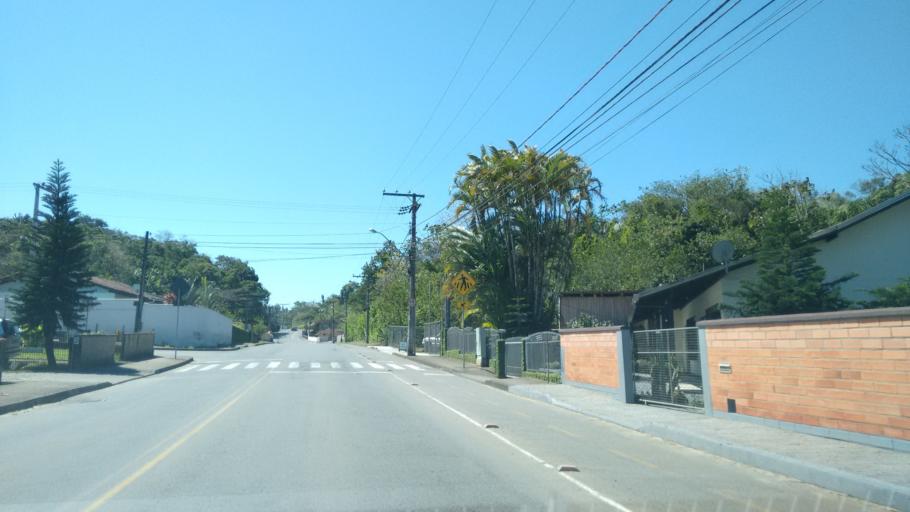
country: BR
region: Santa Catarina
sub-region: Blumenau
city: Blumenau
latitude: -26.8833
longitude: -49.1230
